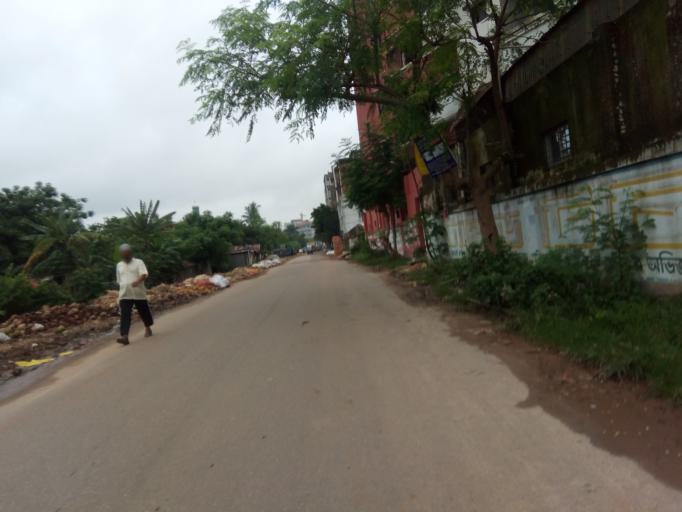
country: BD
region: Dhaka
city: Tungi
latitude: 23.8510
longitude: 90.4145
